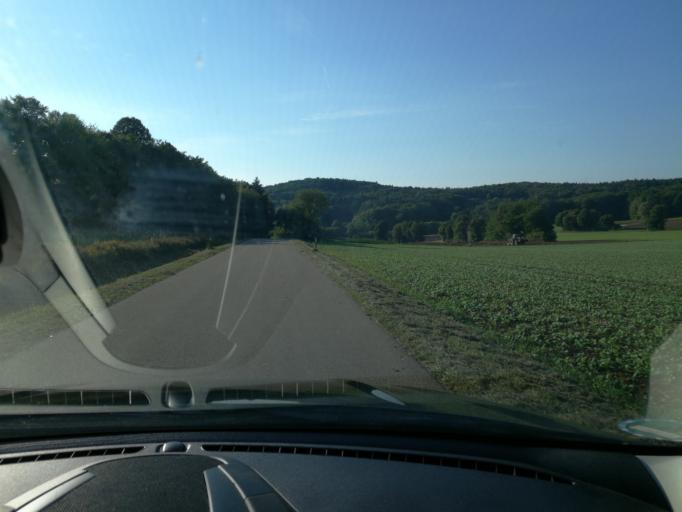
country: DE
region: Bavaria
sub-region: Upper Palatinate
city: Parsberg
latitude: 49.1888
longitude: 11.7217
